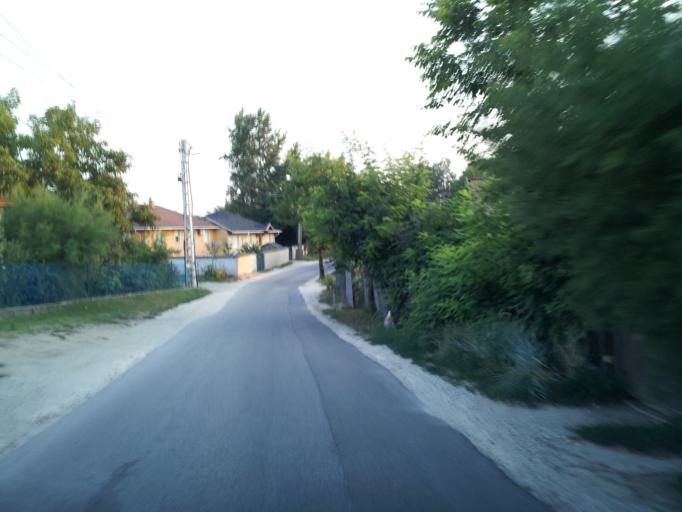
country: HU
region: Pest
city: Szigetszentmiklos
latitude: 47.3264
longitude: 19.0309
